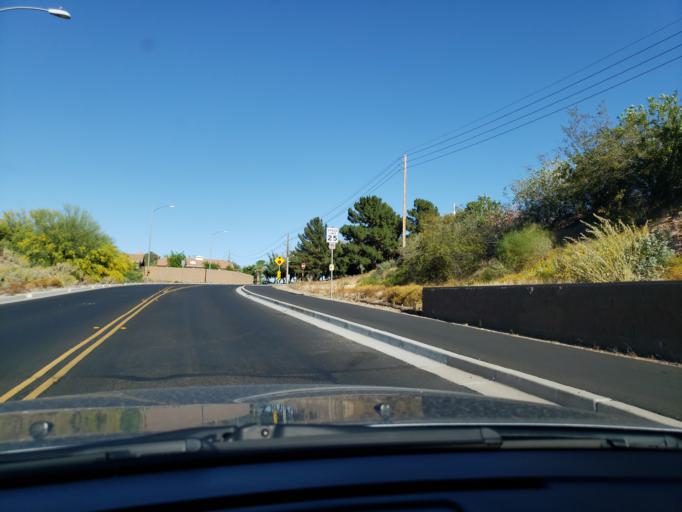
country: US
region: Arizona
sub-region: Maricopa County
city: Youngtown
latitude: 33.5803
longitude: -112.3061
